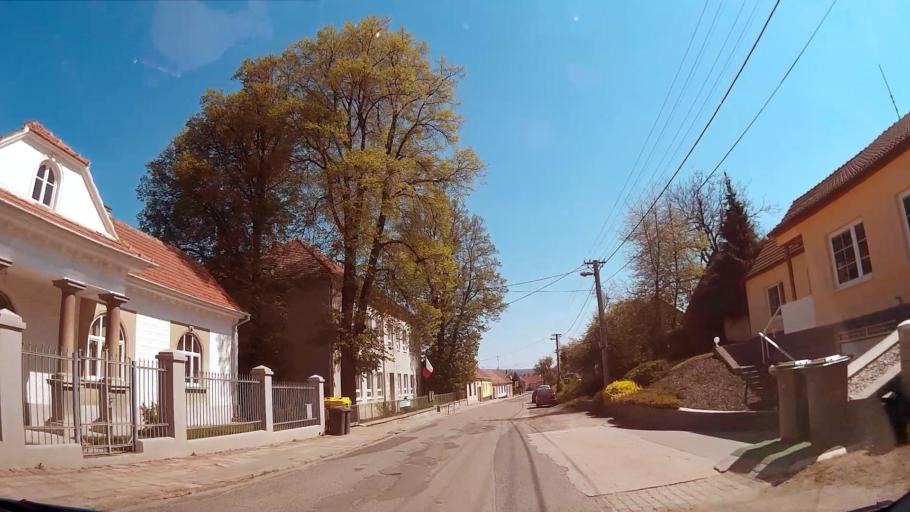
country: CZ
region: South Moravian
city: Moravsky Krumlov
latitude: 49.0848
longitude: 16.3199
